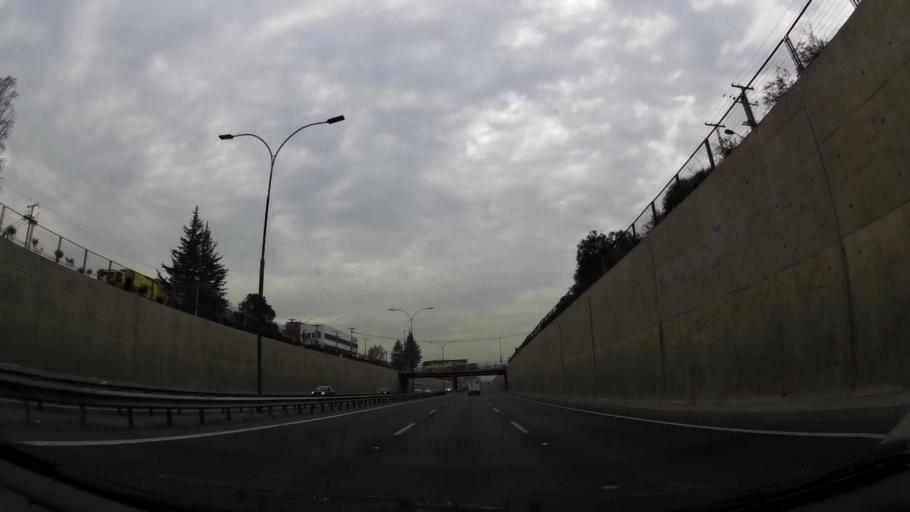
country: CL
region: Santiago Metropolitan
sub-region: Provincia de Santiago
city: Lo Prado
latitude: -33.3908
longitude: -70.6892
